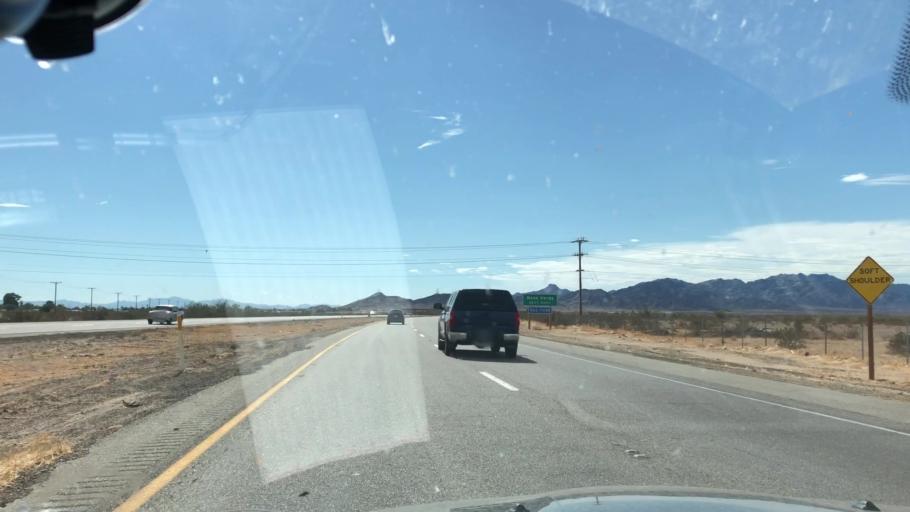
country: US
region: California
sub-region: Riverside County
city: Mesa Verde
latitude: 33.6070
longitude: -114.7128
